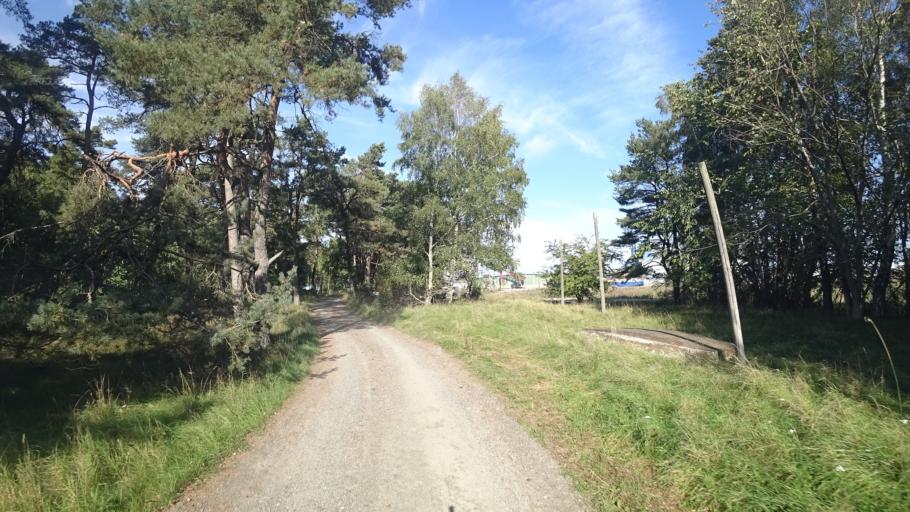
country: SE
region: Skane
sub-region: Kristianstads Kommun
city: Ahus
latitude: 55.9254
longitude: 14.3194
